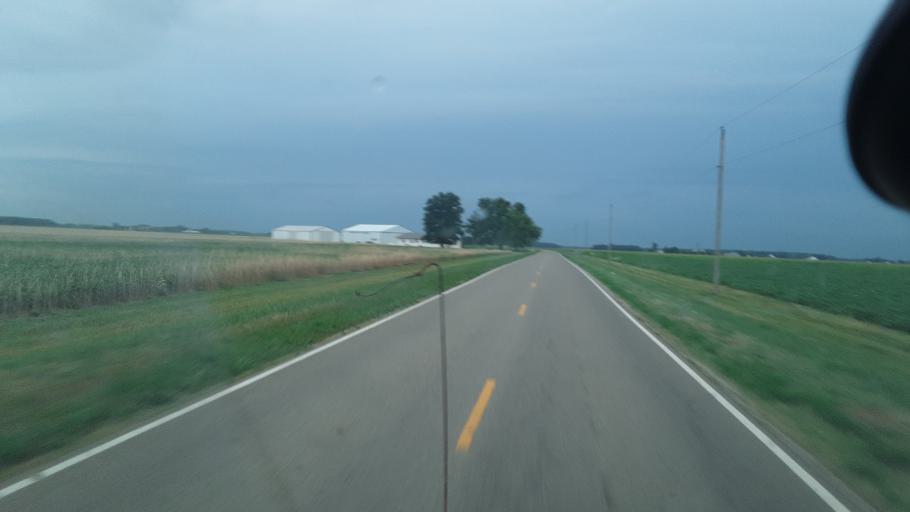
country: US
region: Ohio
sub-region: Defiance County
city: Hicksville
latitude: 41.2757
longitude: -84.7396
